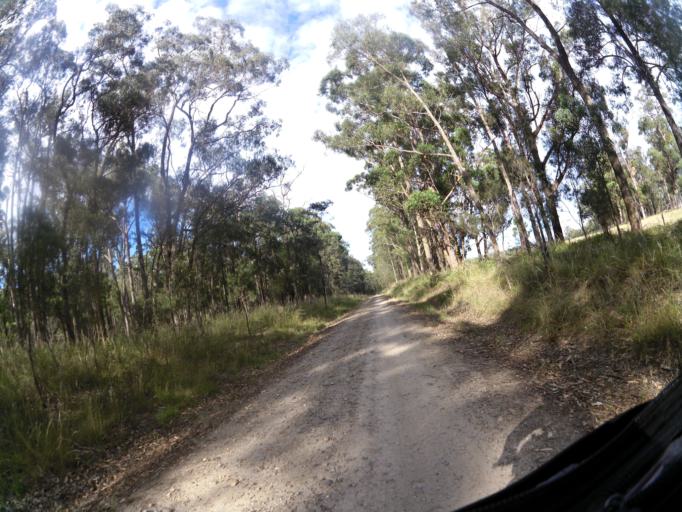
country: AU
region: Victoria
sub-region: East Gippsland
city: Lakes Entrance
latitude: -37.7460
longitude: 148.3670
